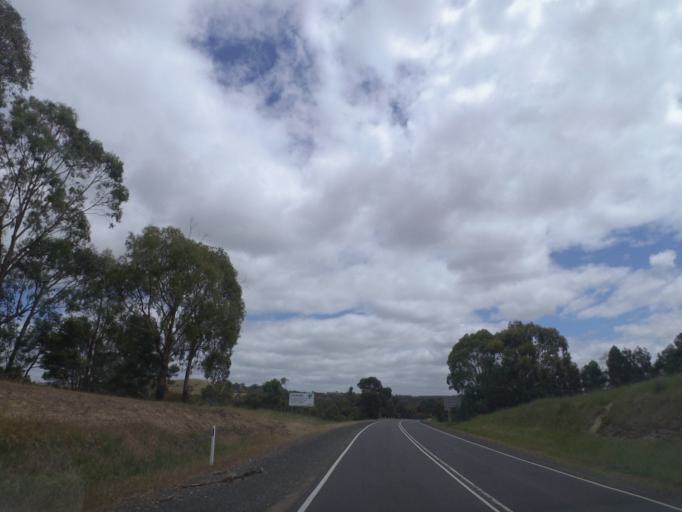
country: AU
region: Victoria
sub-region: Whittlesea
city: Whittlesea
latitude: -37.2857
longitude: 145.0532
